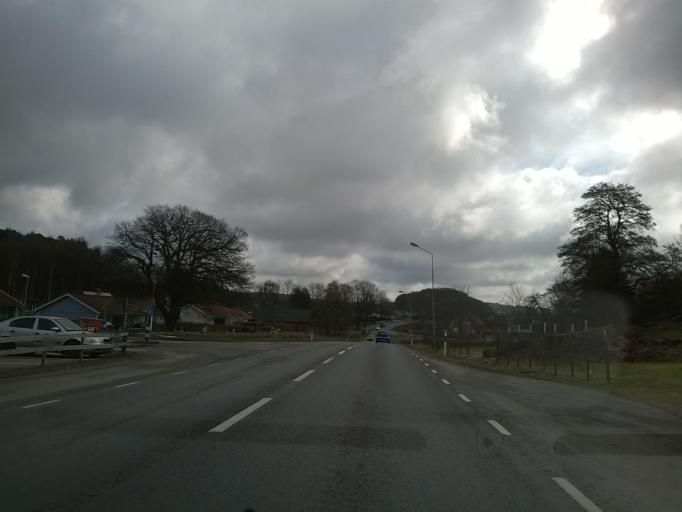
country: SE
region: Halland
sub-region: Varbergs Kommun
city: Tvaaker
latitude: 57.1449
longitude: 12.4532
